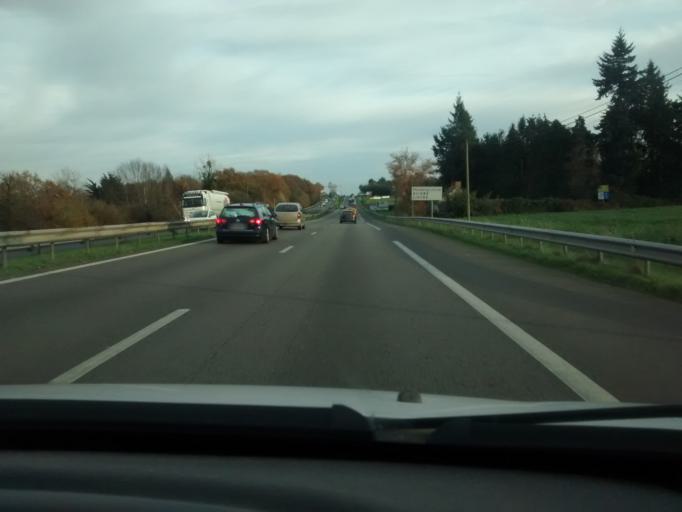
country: FR
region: Brittany
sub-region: Departement d'Ille-et-Vilaine
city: Acigne
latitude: 48.1135
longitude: -1.5523
